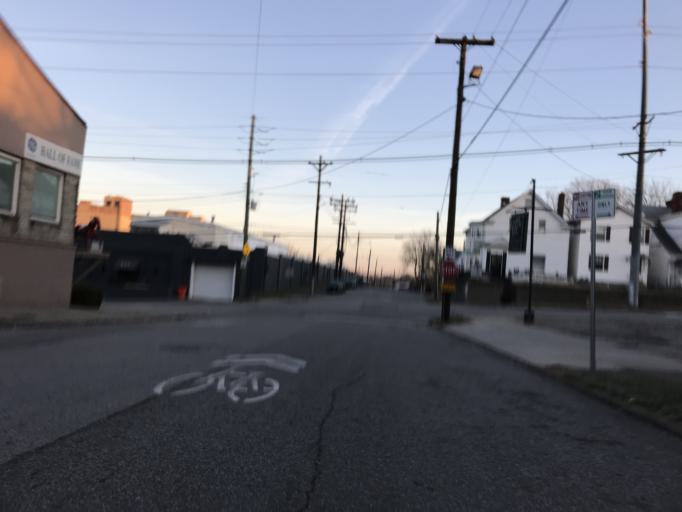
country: US
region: Kentucky
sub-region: Jefferson County
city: Louisville
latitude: 38.2392
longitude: -85.7366
